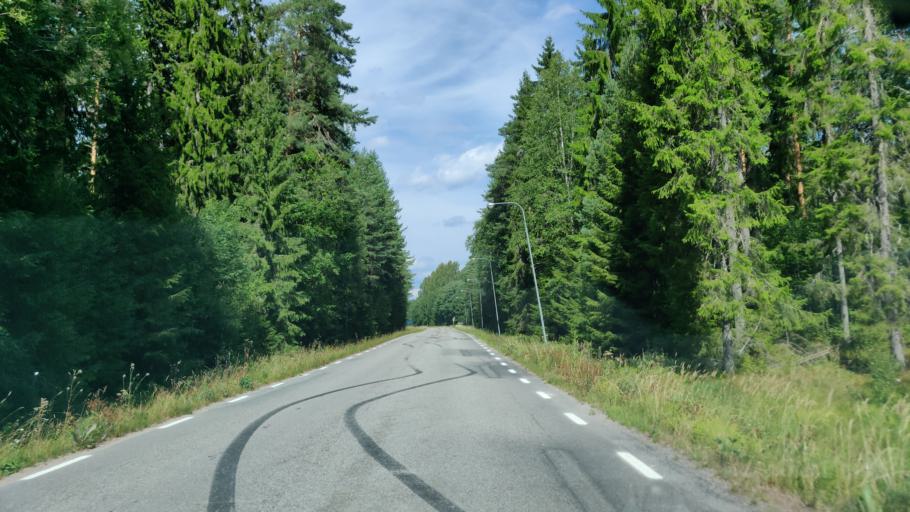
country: SE
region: Vaermland
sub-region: Hagfors Kommun
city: Ekshaerad
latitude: 60.1120
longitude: 13.5017
